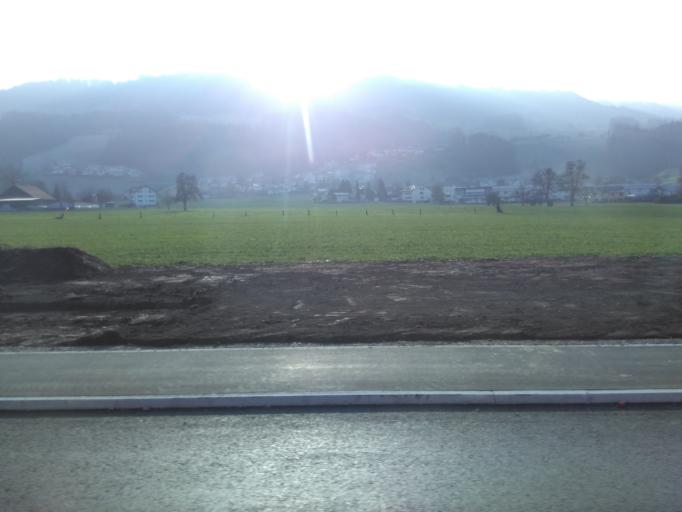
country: CH
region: Schwyz
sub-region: Bezirk March
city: Lachen
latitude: 47.1798
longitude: 8.8828
